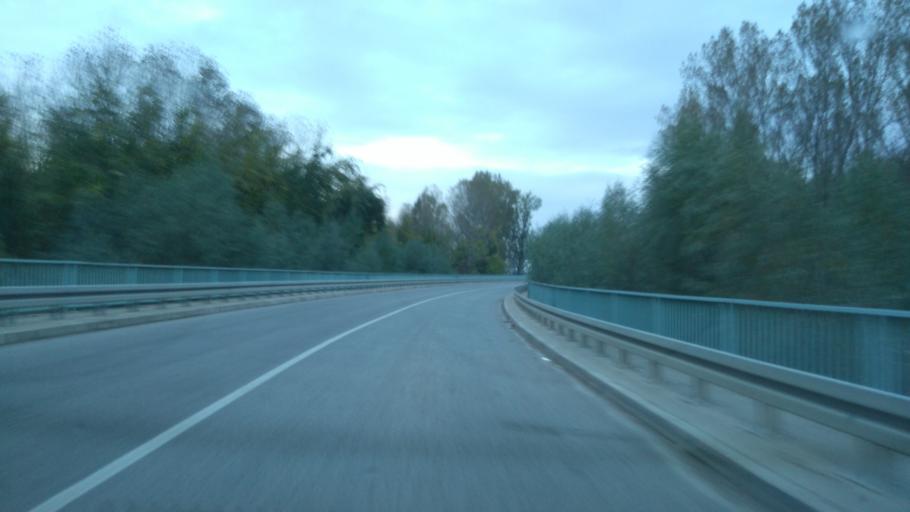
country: RS
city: Mol
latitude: 45.7839
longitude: 20.1515
